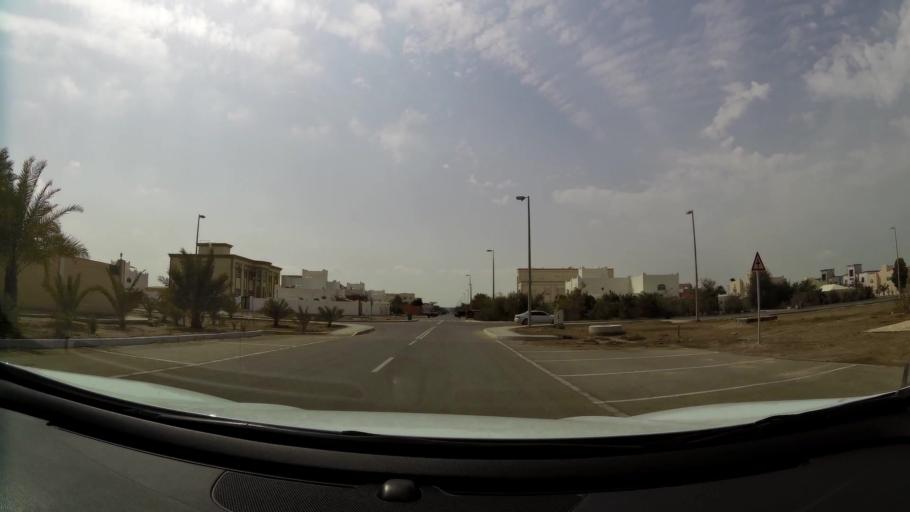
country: AE
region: Abu Dhabi
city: Abu Dhabi
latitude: 24.5483
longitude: 54.6359
